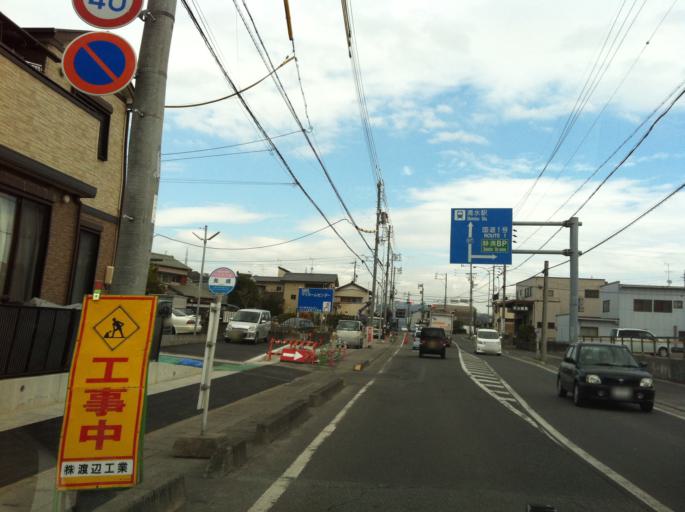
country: JP
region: Shizuoka
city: Shizuoka-shi
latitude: 35.0110
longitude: 138.4312
